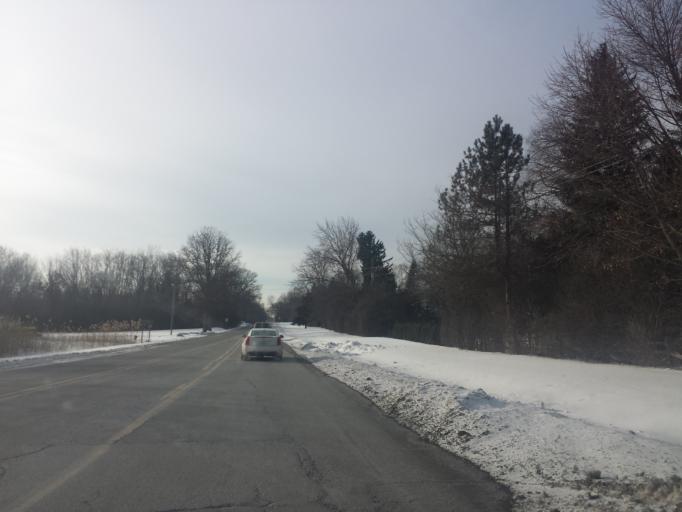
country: US
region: Michigan
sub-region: Oakland County
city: Franklin
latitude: 42.5423
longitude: -83.3411
